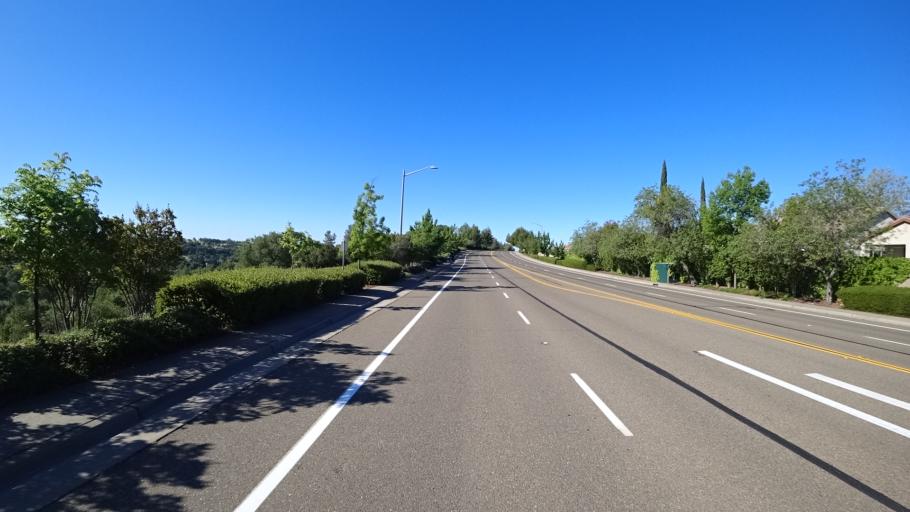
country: US
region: California
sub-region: Placer County
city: Rocklin
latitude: 38.8294
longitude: -121.2320
